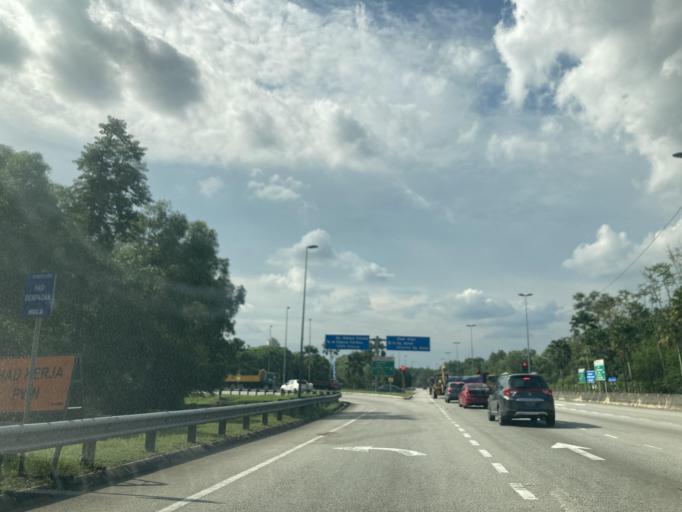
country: MY
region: Selangor
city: Kampung Baru Subang
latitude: 3.1395
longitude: 101.5525
